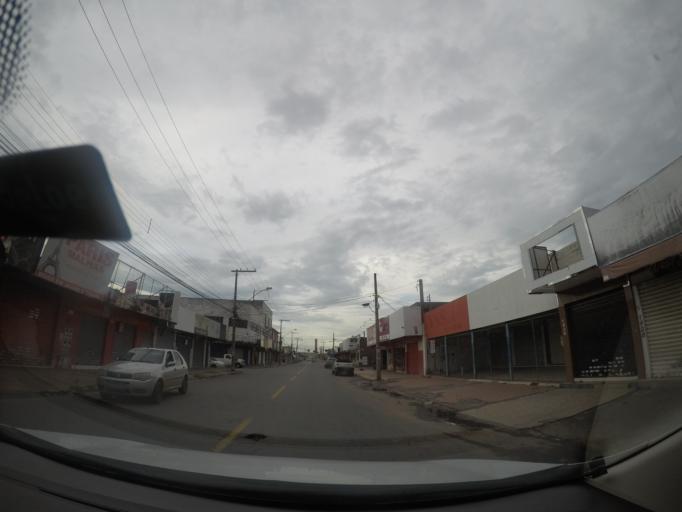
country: BR
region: Goias
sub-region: Goiania
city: Goiania
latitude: -16.6590
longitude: -49.2719
